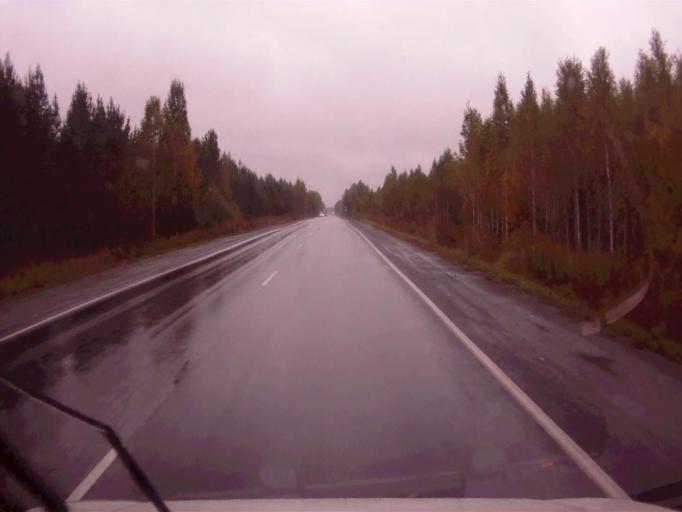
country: RU
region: Chelyabinsk
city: Tayginka
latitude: 55.5385
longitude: 60.6466
